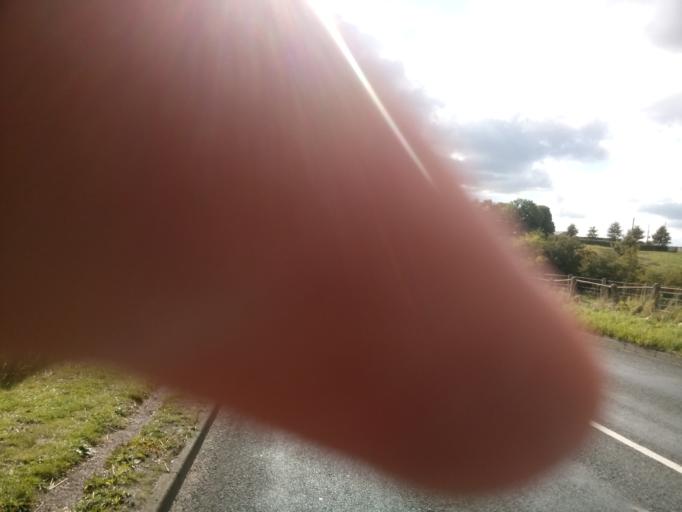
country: GB
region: England
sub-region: County Durham
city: Pittington
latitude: 54.7848
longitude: -1.5033
